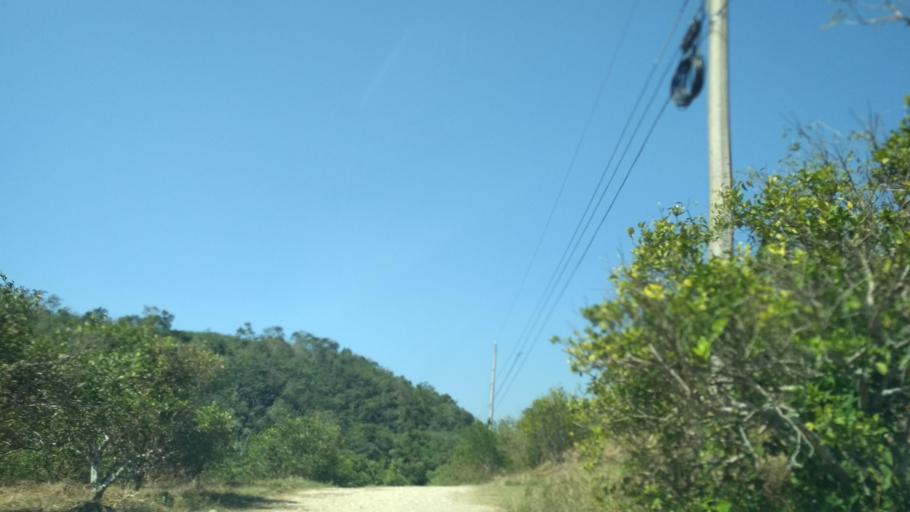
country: MX
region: Veracruz
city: Gutierrez Zamora
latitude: 20.4748
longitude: -97.1557
